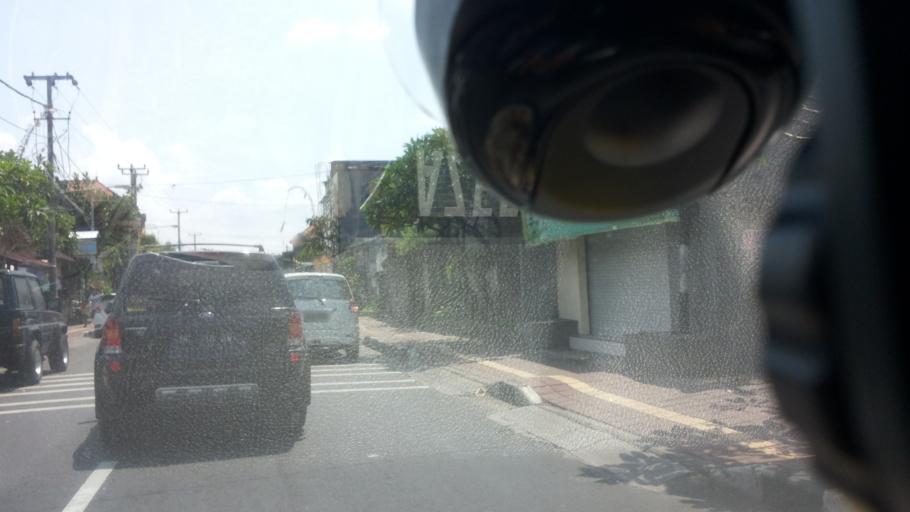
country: ID
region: Bali
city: Denpasar
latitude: -8.6538
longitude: 115.2086
